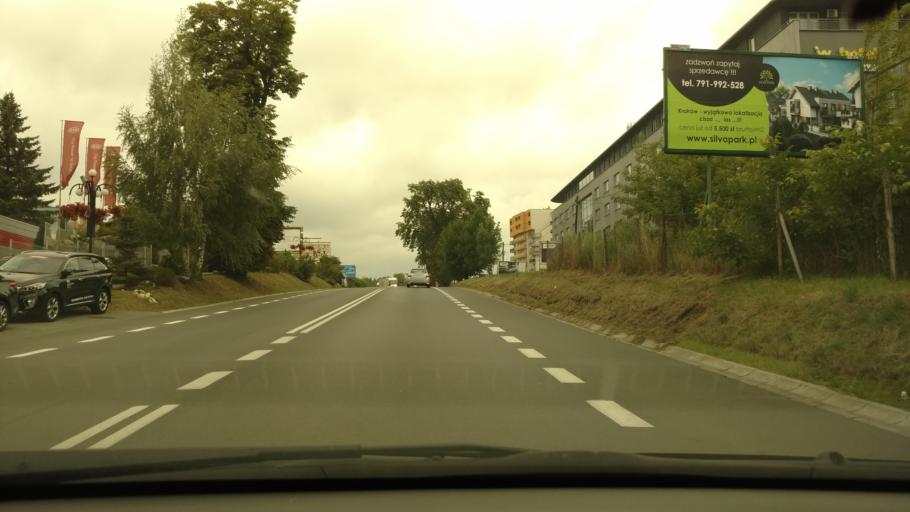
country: PL
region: Lesser Poland Voivodeship
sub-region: Krakow
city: Krakow
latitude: 50.0990
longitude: 19.9626
